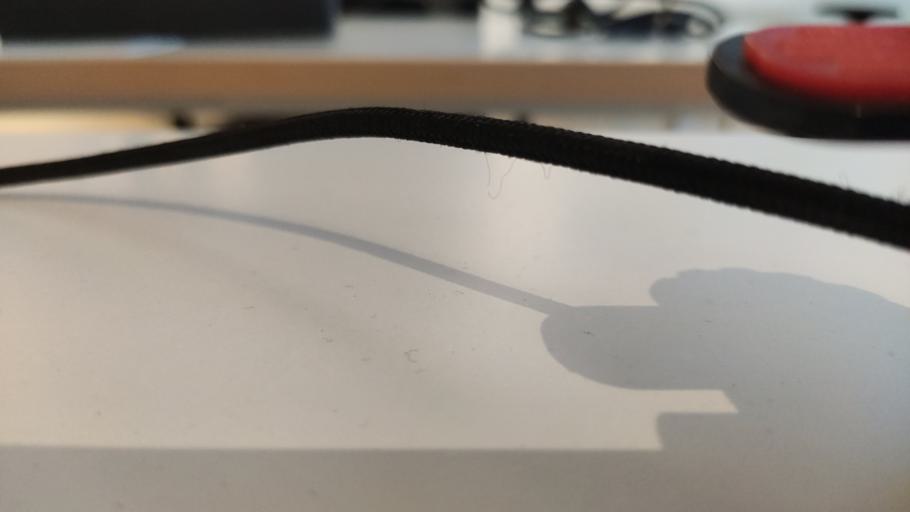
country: RU
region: Moskovskaya
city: Novopetrovskoye
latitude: 55.8777
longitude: 36.4097
